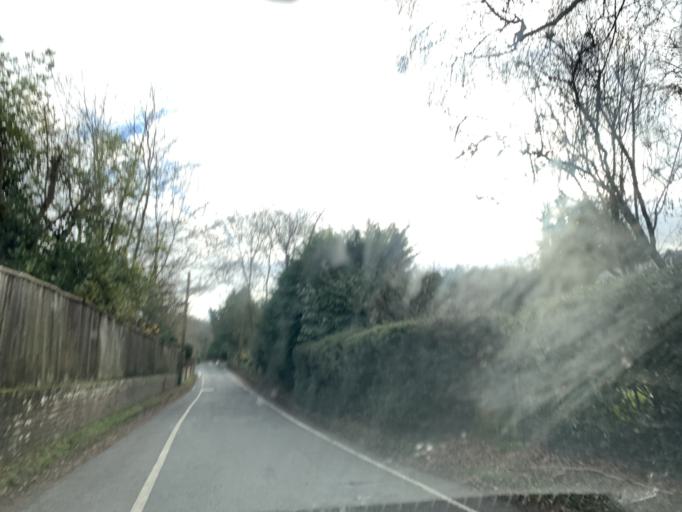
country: GB
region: England
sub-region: Hampshire
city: Lyndhurst
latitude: 50.8759
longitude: -1.5966
